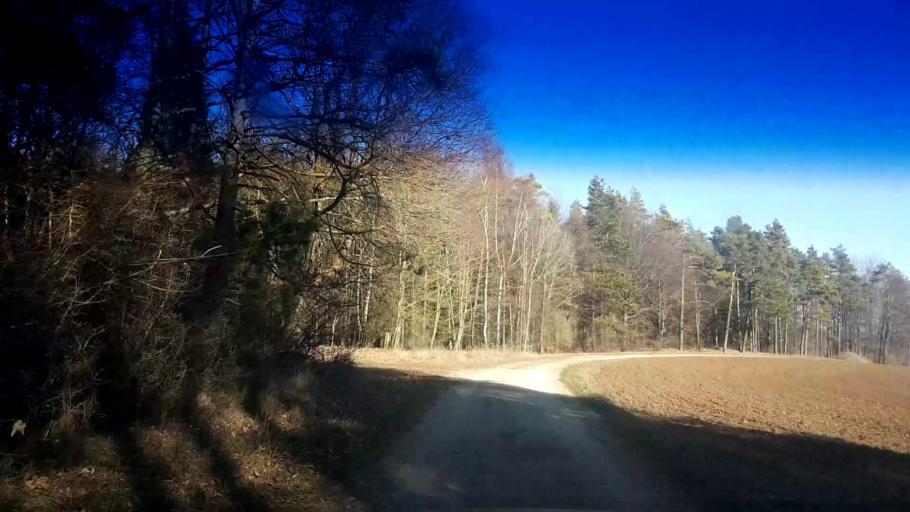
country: DE
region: Bavaria
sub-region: Upper Franconia
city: Poxdorf
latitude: 49.9669
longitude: 11.0825
